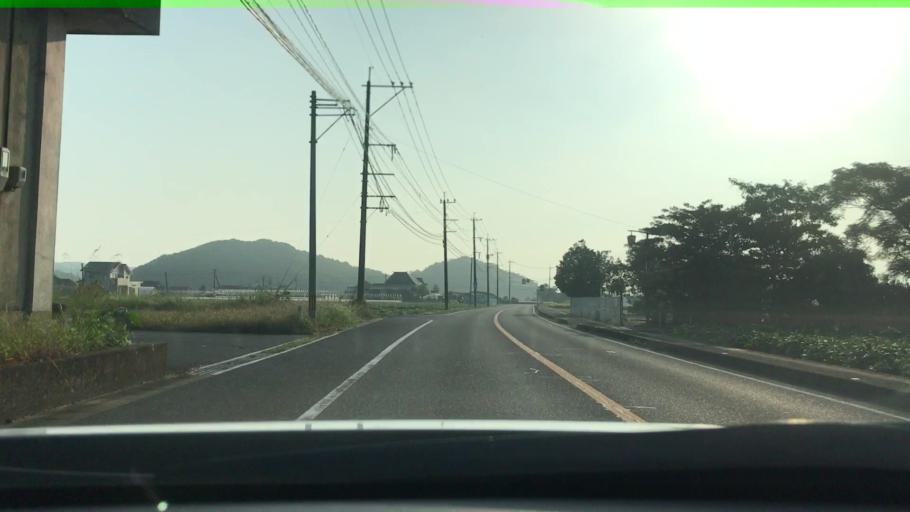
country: JP
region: Saga Prefecture
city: Takeocho-takeo
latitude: 33.2089
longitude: 130.0725
